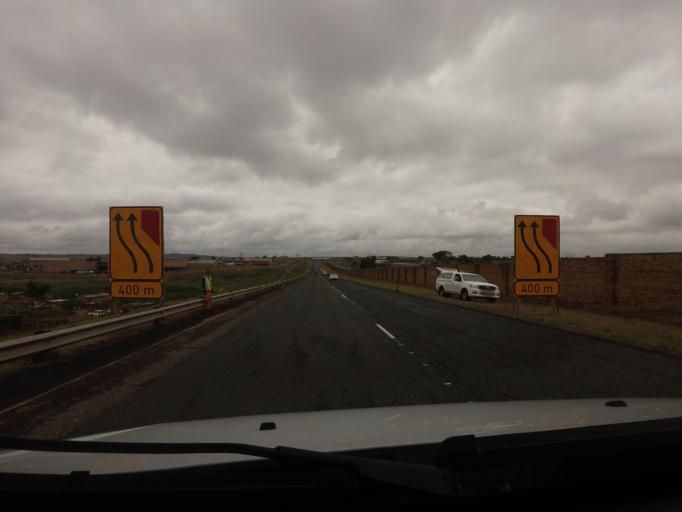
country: ZA
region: Mpumalanga
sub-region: Nkangala District Municipality
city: Witbank
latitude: -25.8735
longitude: 29.1266
